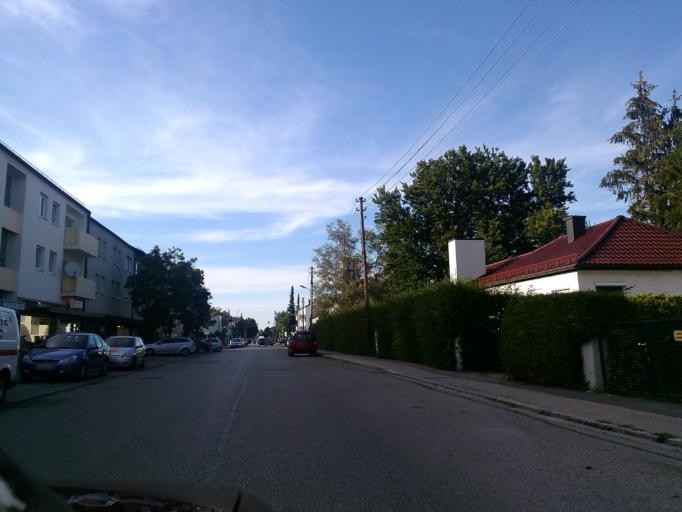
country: DE
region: Bavaria
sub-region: Upper Bavaria
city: Germering
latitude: 48.1213
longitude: 11.3669
